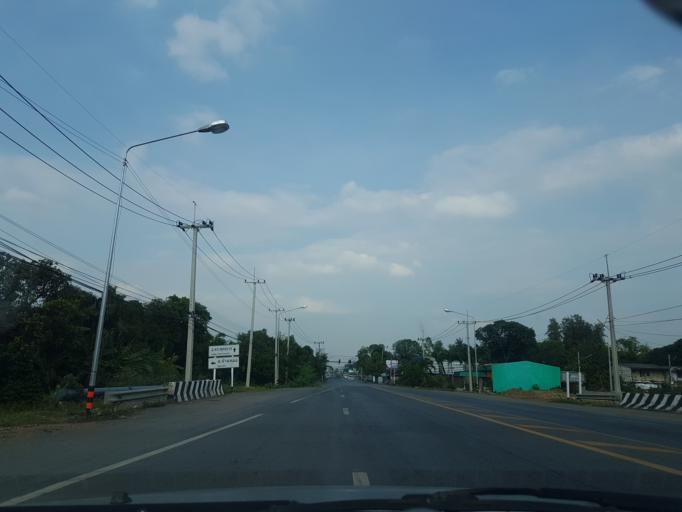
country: TH
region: Sara Buri
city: Ban Mo
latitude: 14.6050
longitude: 100.7370
